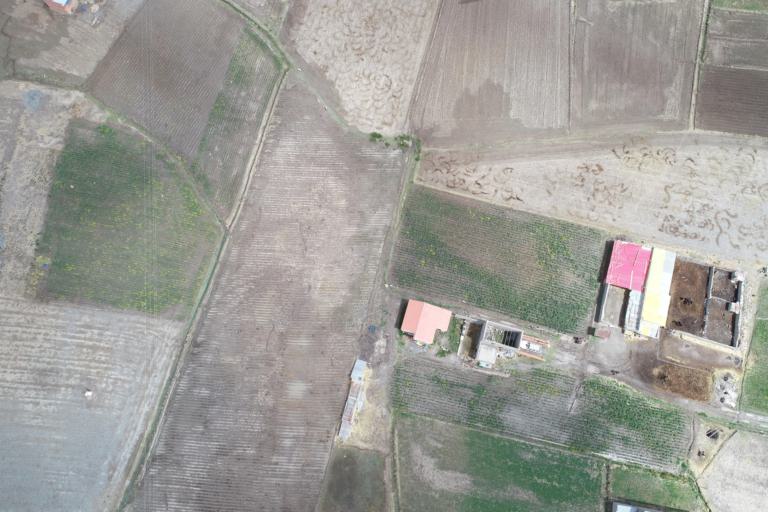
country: BO
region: La Paz
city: Achacachi
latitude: -16.0316
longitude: -68.6860
